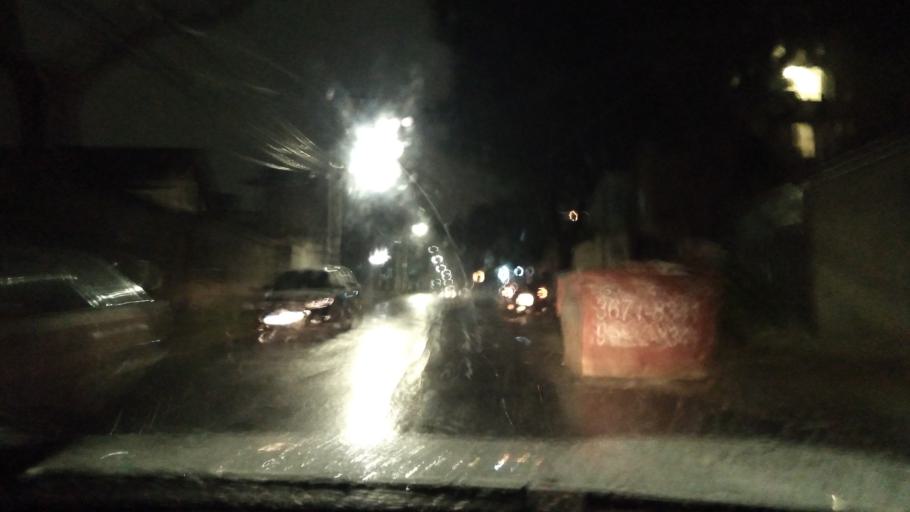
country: BR
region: Minas Gerais
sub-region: Belo Horizonte
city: Belo Horizonte
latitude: -19.8785
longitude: -43.9401
